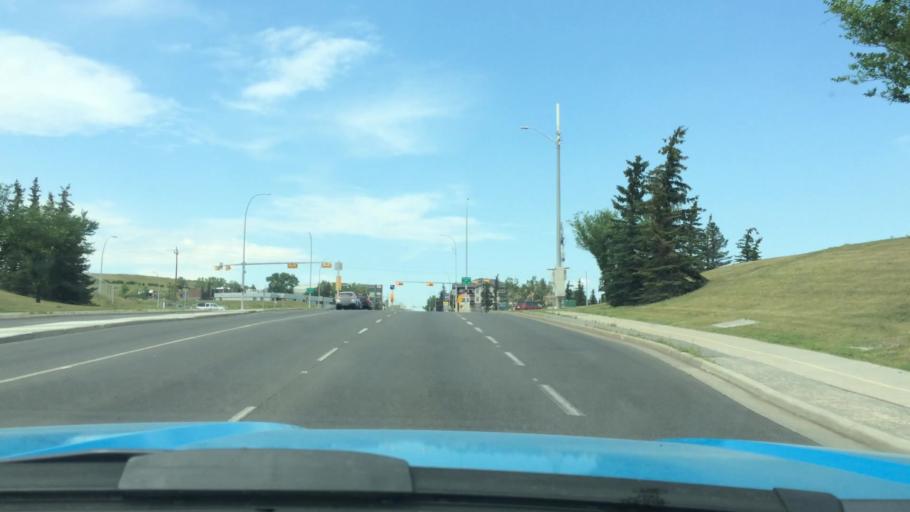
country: CA
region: Alberta
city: Calgary
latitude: 51.0885
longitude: -114.0946
